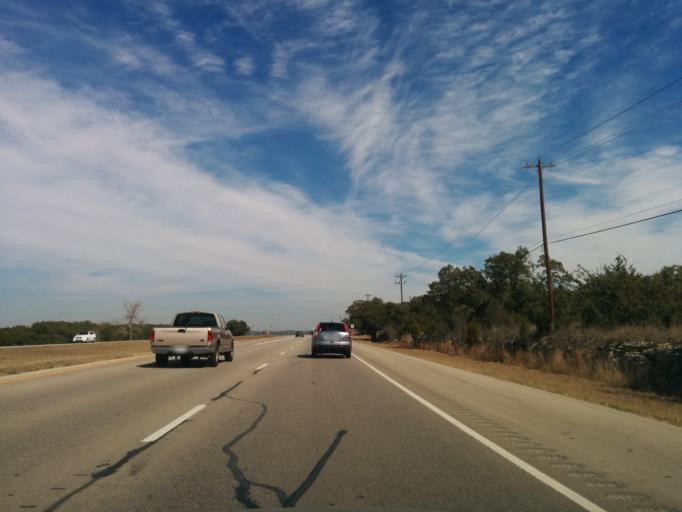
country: US
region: Texas
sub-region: Comal County
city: Bulverde
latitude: 29.8212
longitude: -98.4174
